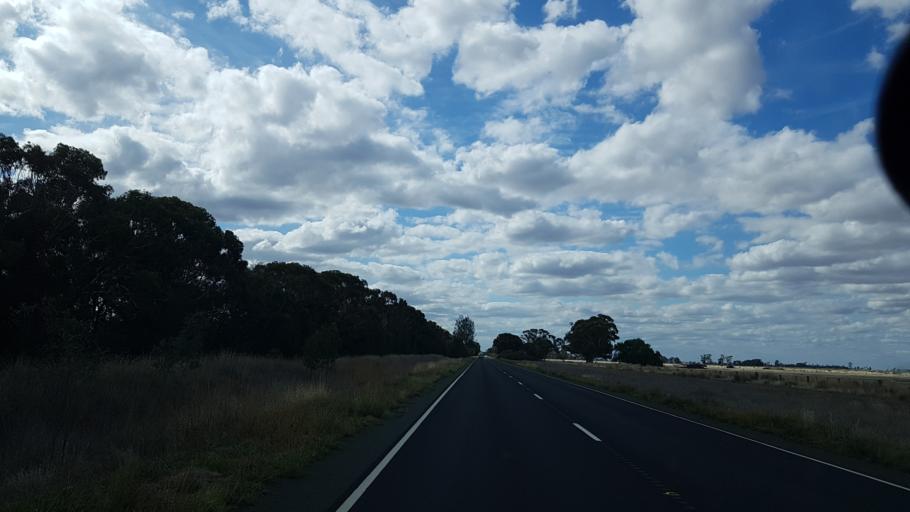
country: AU
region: Victoria
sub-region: Swan Hill
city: Swan Hill
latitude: -35.9839
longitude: 143.9454
